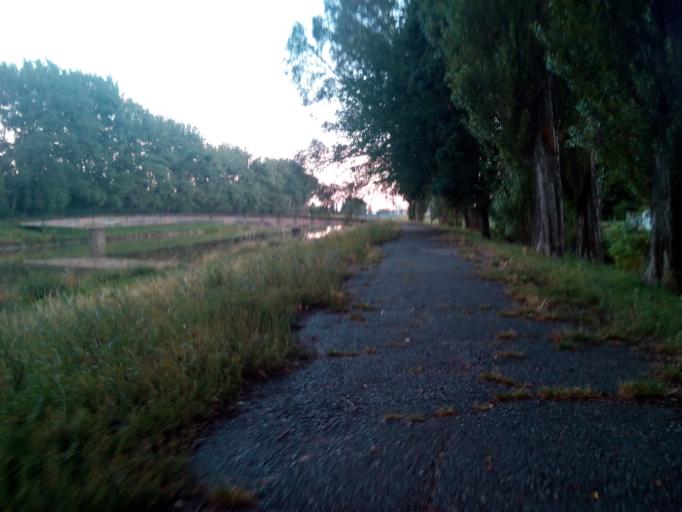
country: SK
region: Kosicky
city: Kosice
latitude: 48.7487
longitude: 21.2550
